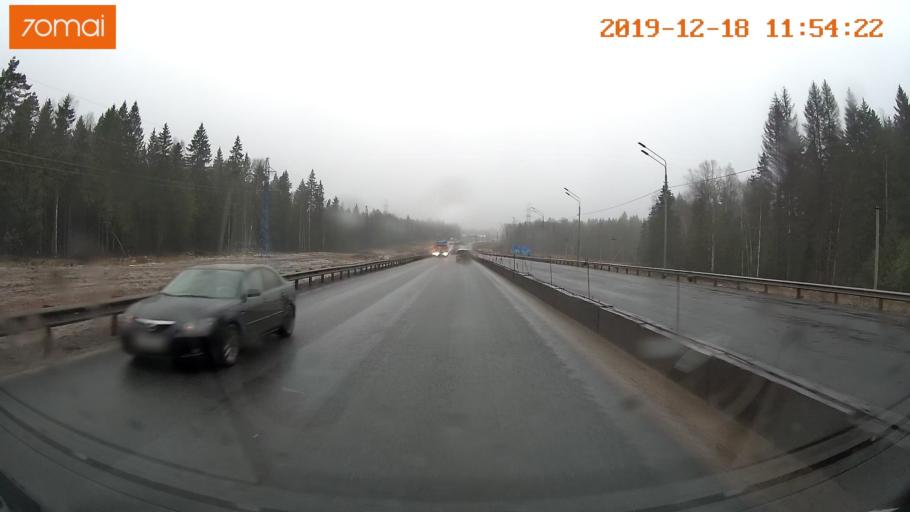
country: RU
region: Moskovskaya
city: Yershovo
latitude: 55.8151
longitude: 36.9173
